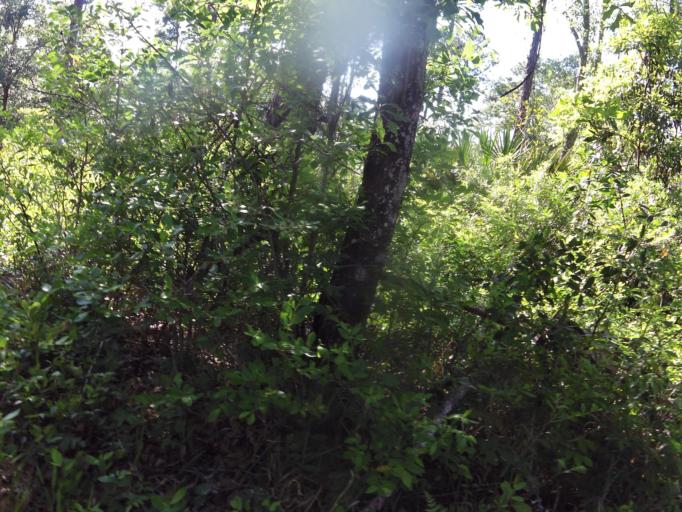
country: US
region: Florida
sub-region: Saint Johns County
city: Palm Valley
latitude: 30.1337
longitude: -81.3719
